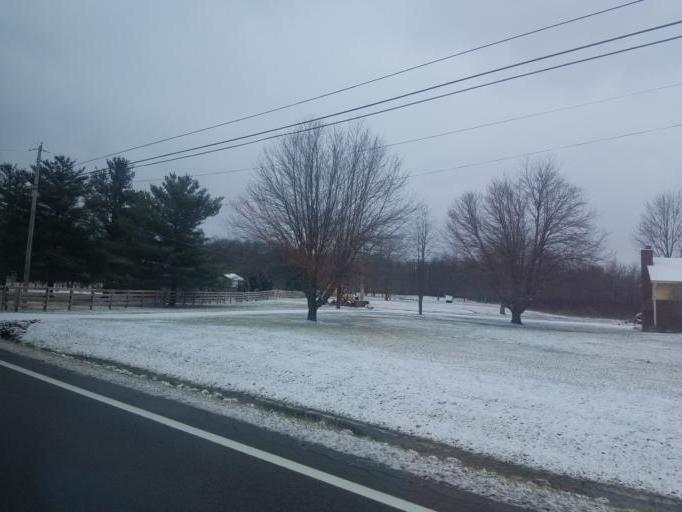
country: US
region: Ohio
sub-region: Licking County
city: Johnstown
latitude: 40.1824
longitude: -82.7454
